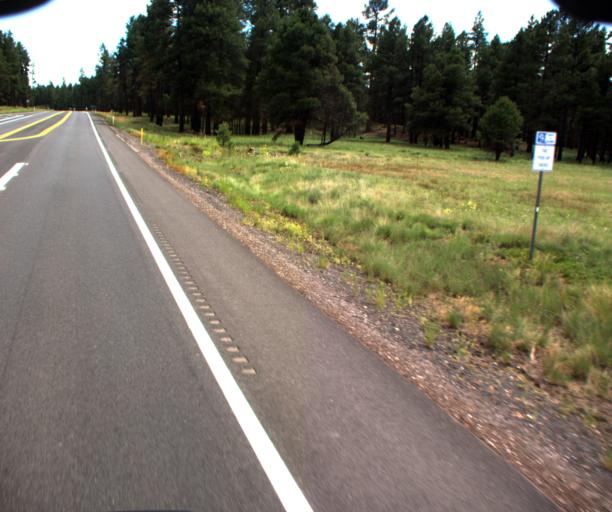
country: US
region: Arizona
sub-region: Coconino County
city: Flagstaff
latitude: 35.2647
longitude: -111.7052
